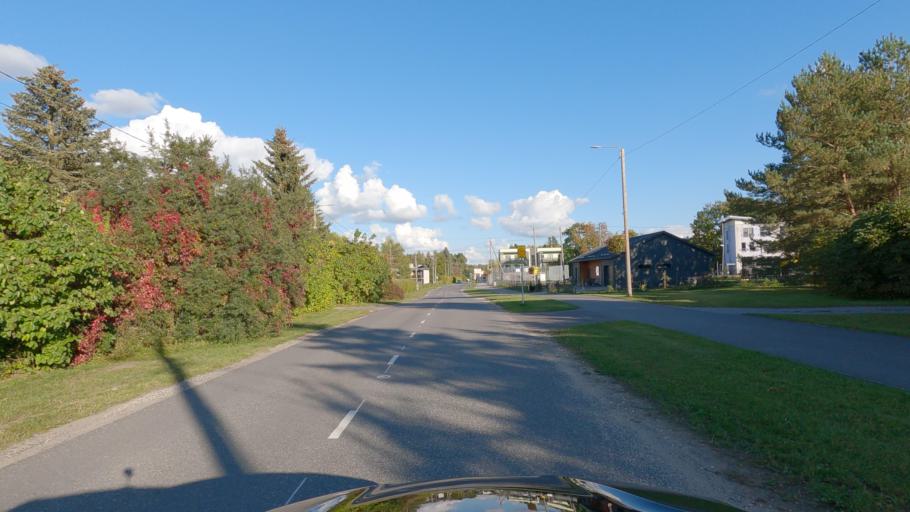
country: EE
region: Harju
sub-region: Saue vald
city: Laagri
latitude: 59.3506
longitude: 24.6317
